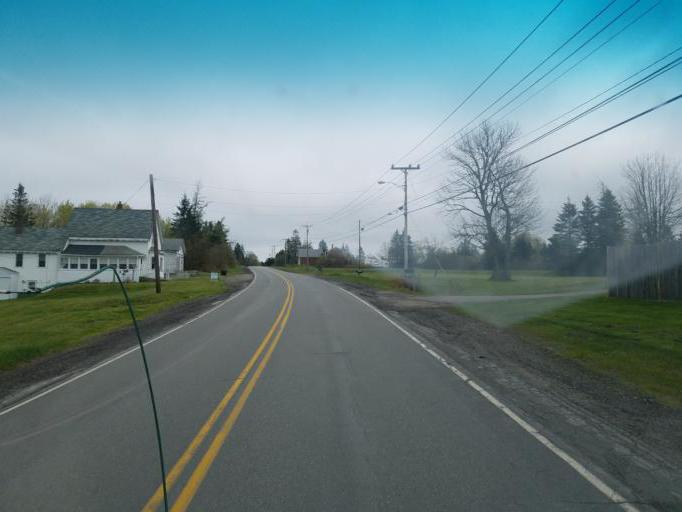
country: US
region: Maine
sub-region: Washington County
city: Eastport
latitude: 44.8221
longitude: -67.0487
